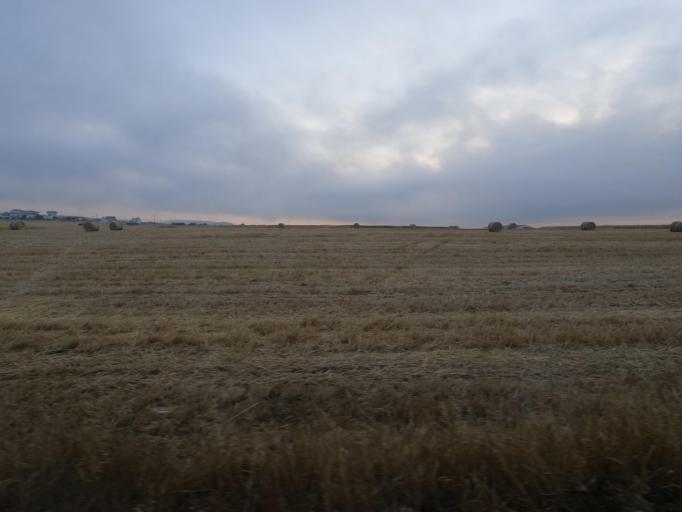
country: CY
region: Larnaka
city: Tersefanou
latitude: 34.8313
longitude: 33.5129
